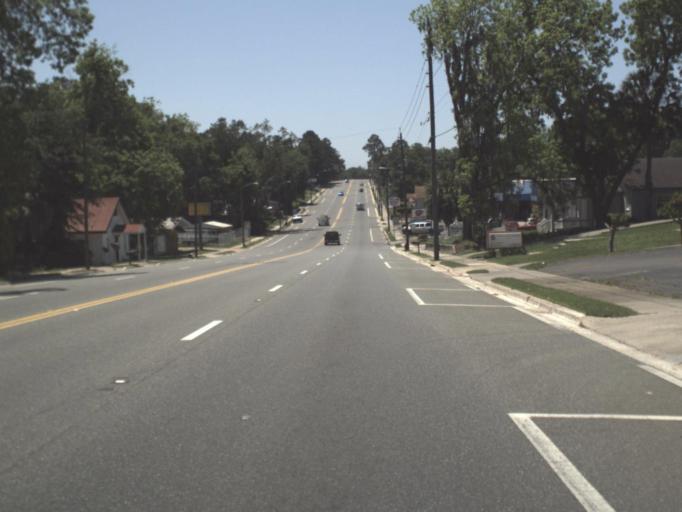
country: US
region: Florida
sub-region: Jefferson County
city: Monticello
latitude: 30.5429
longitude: -83.8702
